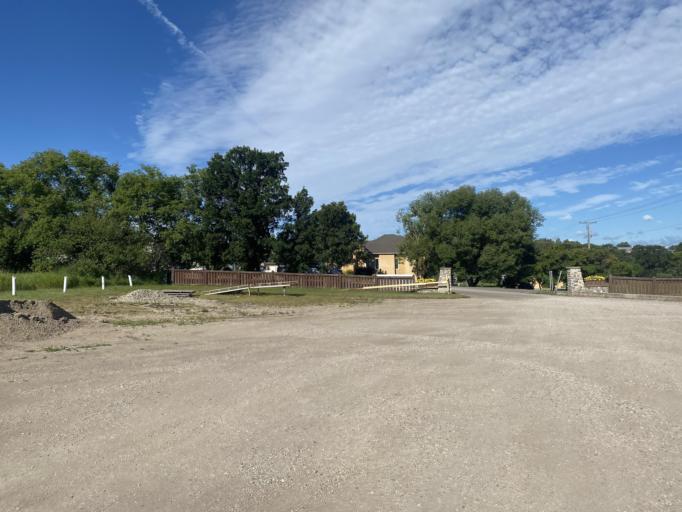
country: CA
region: Manitoba
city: Neepawa
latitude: 50.2334
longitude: -99.4538
